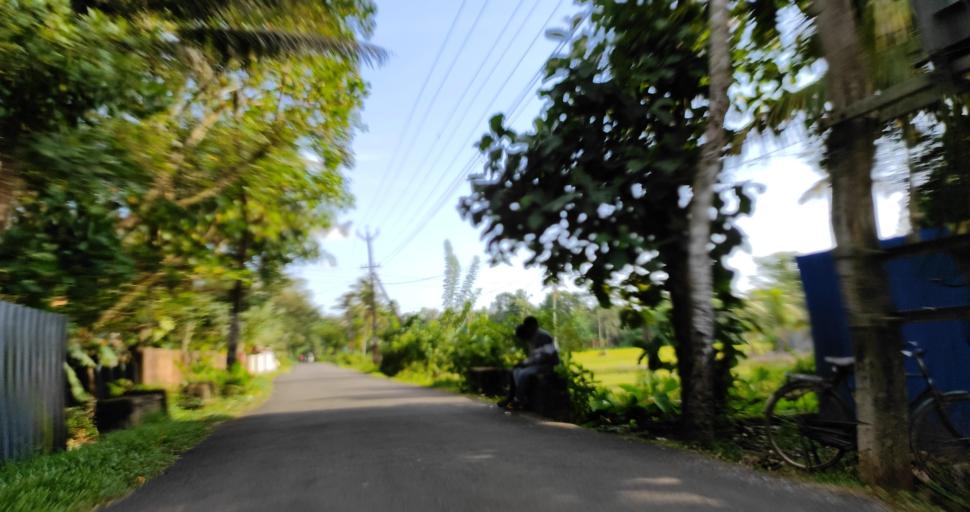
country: IN
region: Kerala
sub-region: Alappuzha
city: Shertallai
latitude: 9.6165
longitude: 76.3410
